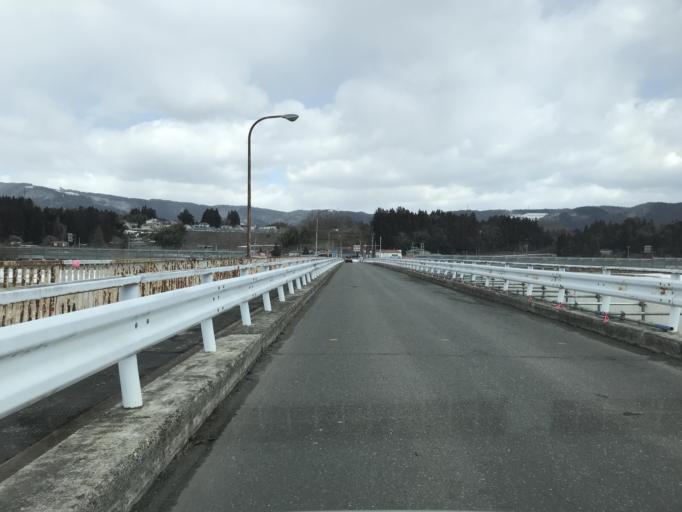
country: JP
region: Miyagi
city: Furukawa
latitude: 38.7329
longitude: 140.7684
